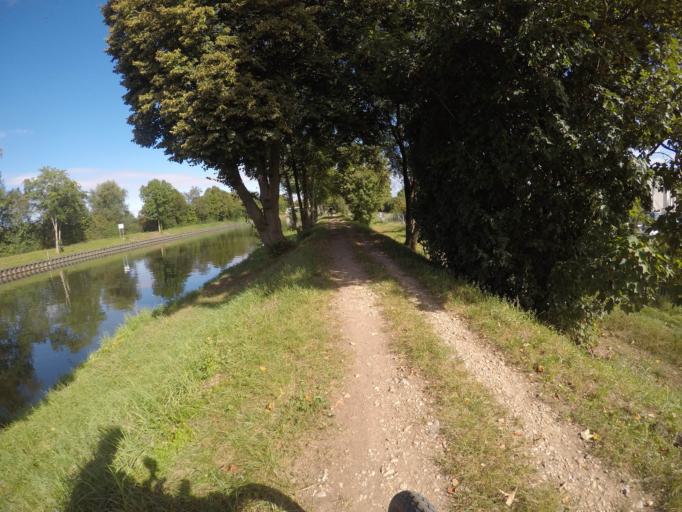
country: DE
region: Baden-Wuerttemberg
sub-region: Regierungsbezirk Stuttgart
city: Pleidelsheim
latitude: 48.9519
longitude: 9.1924
